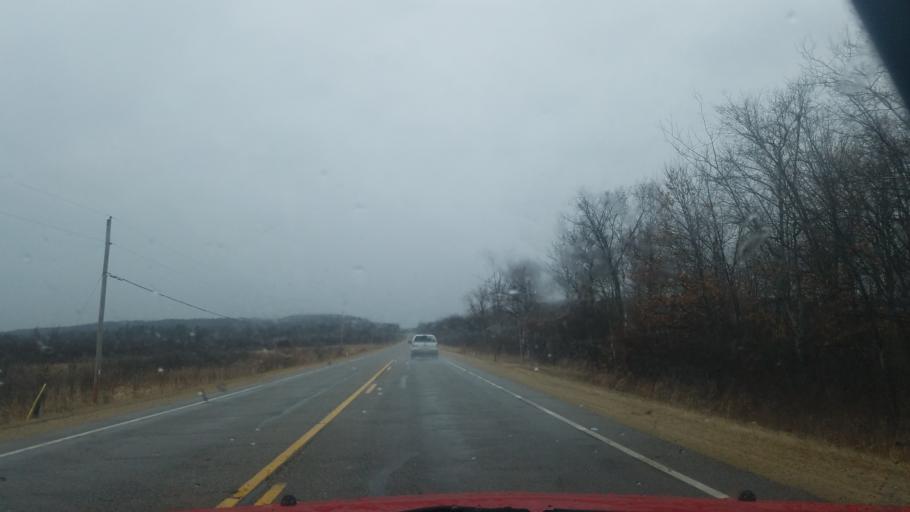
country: US
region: Wisconsin
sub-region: Dunn County
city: Tainter Lake
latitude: 45.0057
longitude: -91.8944
